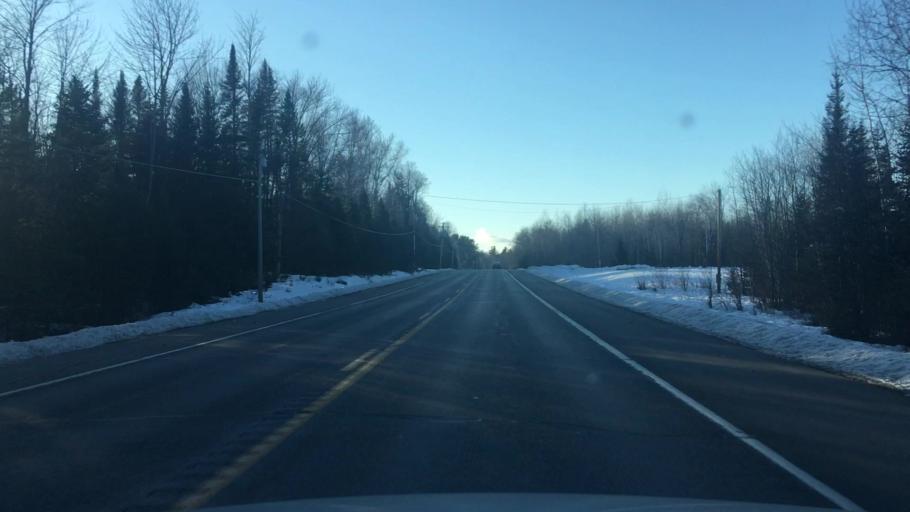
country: US
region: Maine
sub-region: Kennebec County
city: Rome
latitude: 44.6786
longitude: -69.9153
